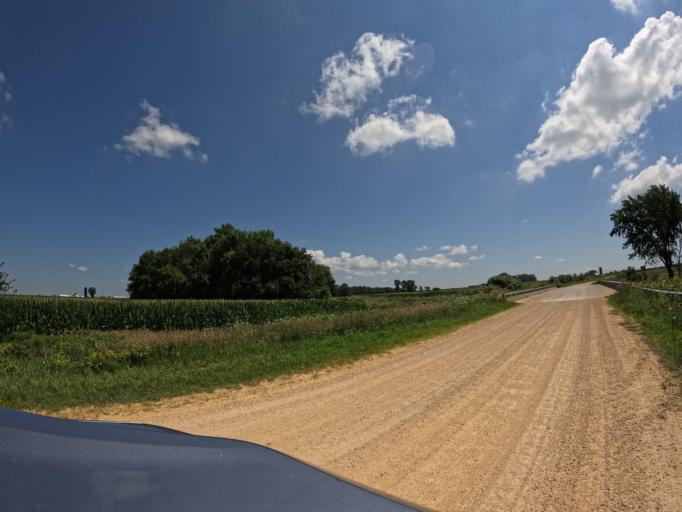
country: US
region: Iowa
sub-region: Clinton County
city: De Witt
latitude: 41.7813
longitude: -90.4313
